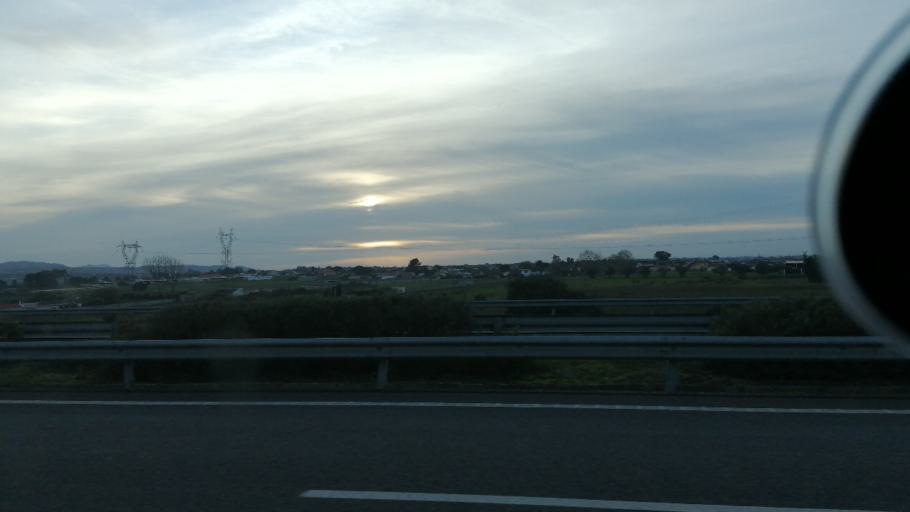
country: PT
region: Setubal
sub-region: Palmela
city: Pinhal Novo
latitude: 38.6325
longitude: -8.8670
